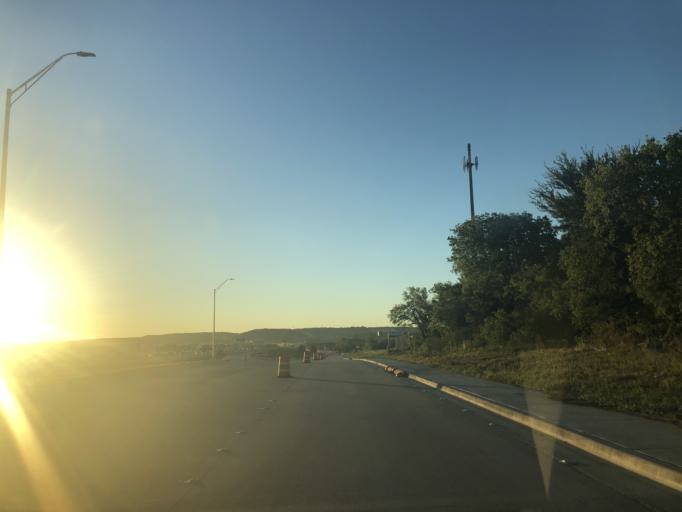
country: US
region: Texas
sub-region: Dallas County
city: Grand Prairie
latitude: 32.6726
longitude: -96.9909
